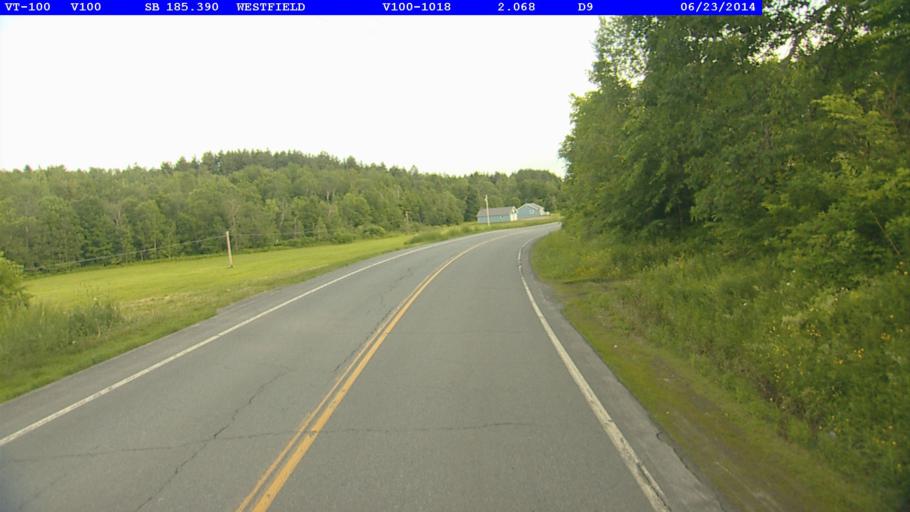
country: US
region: Vermont
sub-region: Orleans County
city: Newport
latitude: 44.8646
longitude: -72.4332
